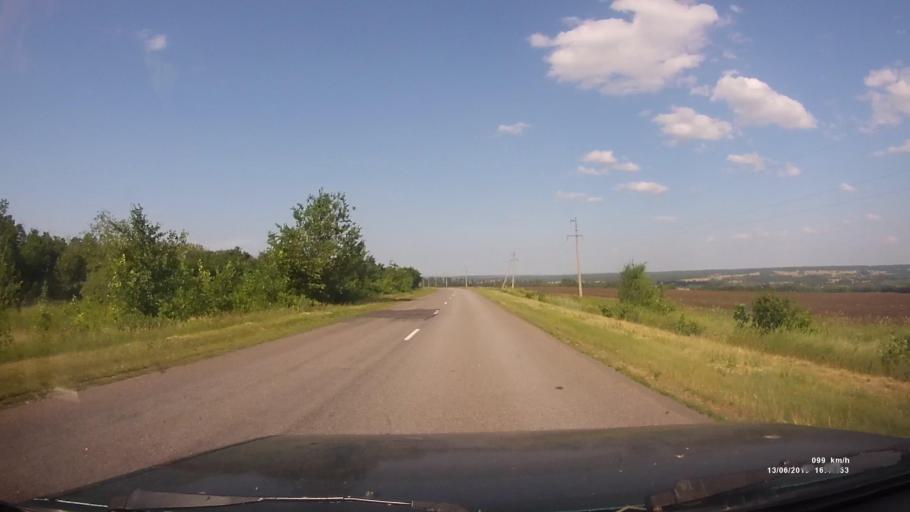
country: RU
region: Rostov
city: Kazanskaya
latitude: 49.9382
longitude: 41.3930
